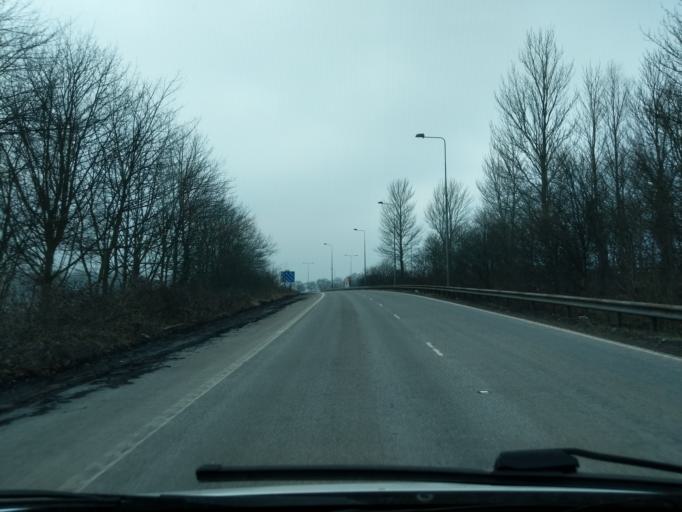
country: GB
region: England
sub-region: Manchester
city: Swinton
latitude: 53.4856
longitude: -2.3803
